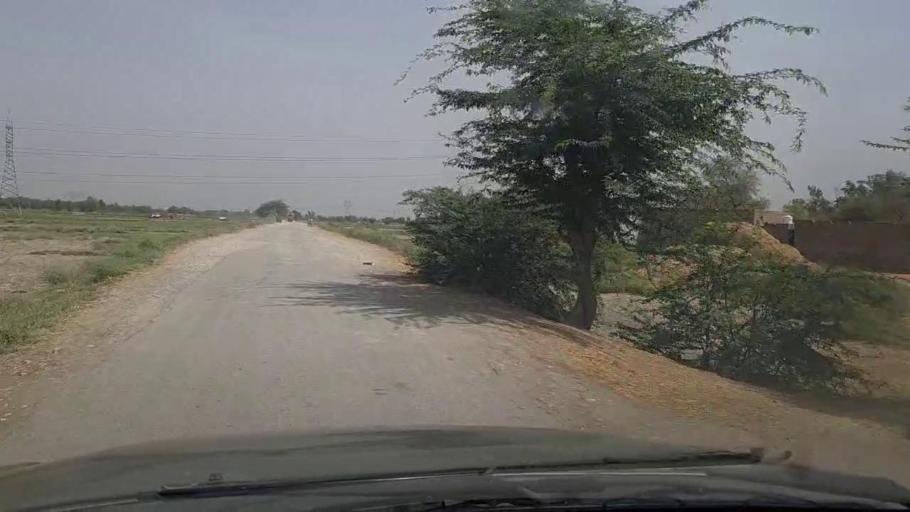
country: PK
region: Sindh
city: Shikarpur
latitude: 27.9240
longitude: 68.6704
